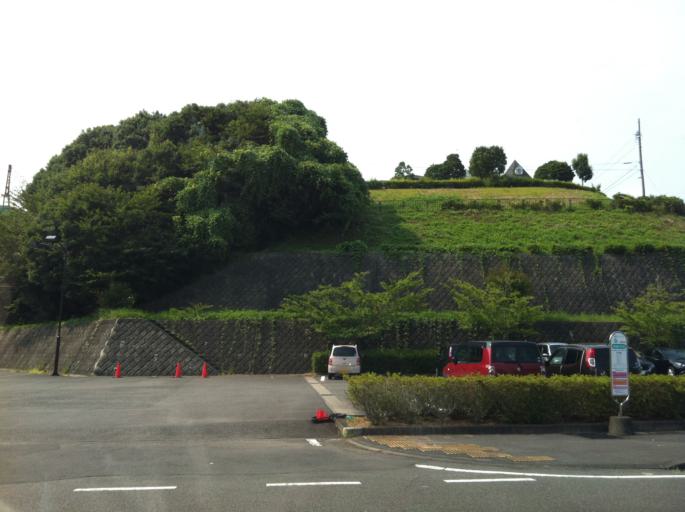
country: JP
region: Shizuoka
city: Shimada
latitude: 34.8511
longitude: 138.1745
